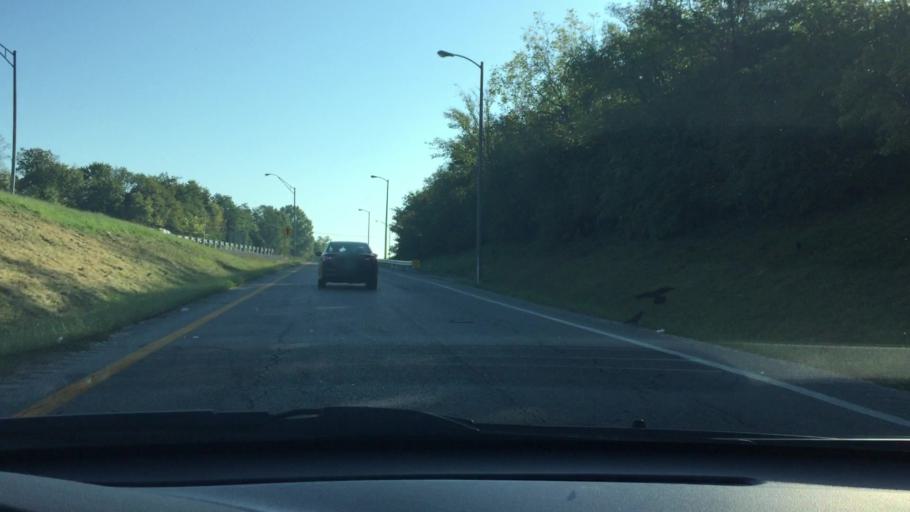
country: US
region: Kentucky
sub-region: Fayette County
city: Lexington
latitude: 37.9908
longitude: -84.4930
